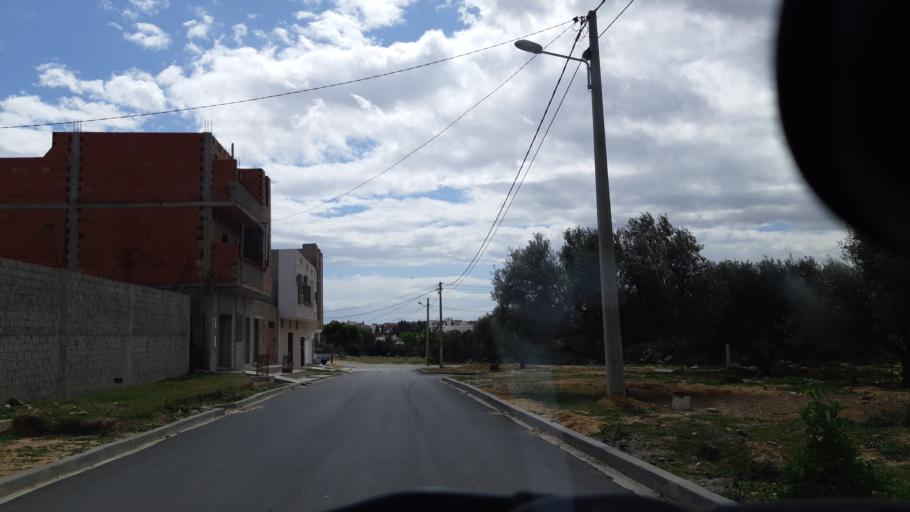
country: TN
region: Susah
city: Akouda
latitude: 35.8781
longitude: 10.5162
